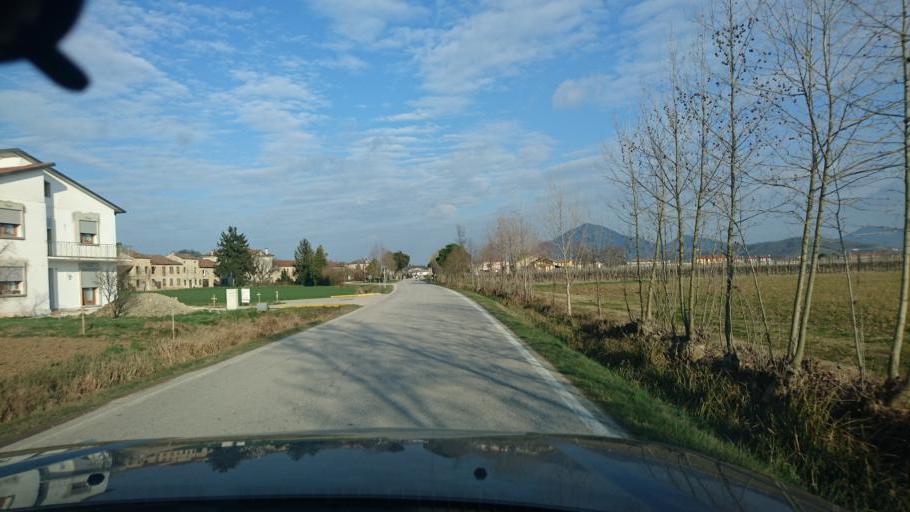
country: IT
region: Veneto
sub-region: Provincia di Vicenza
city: Albettone
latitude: 45.3569
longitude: 11.5709
